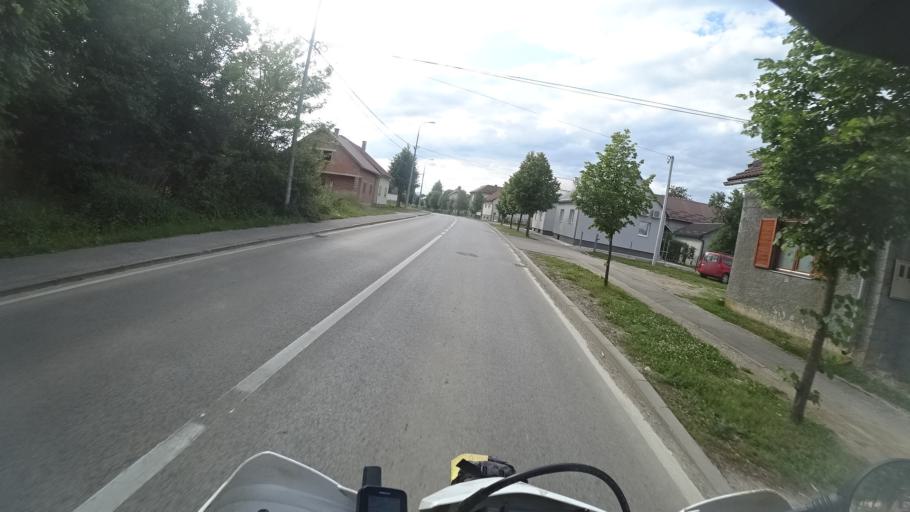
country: HR
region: Licko-Senjska
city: Gospic
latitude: 44.5399
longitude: 15.3835
